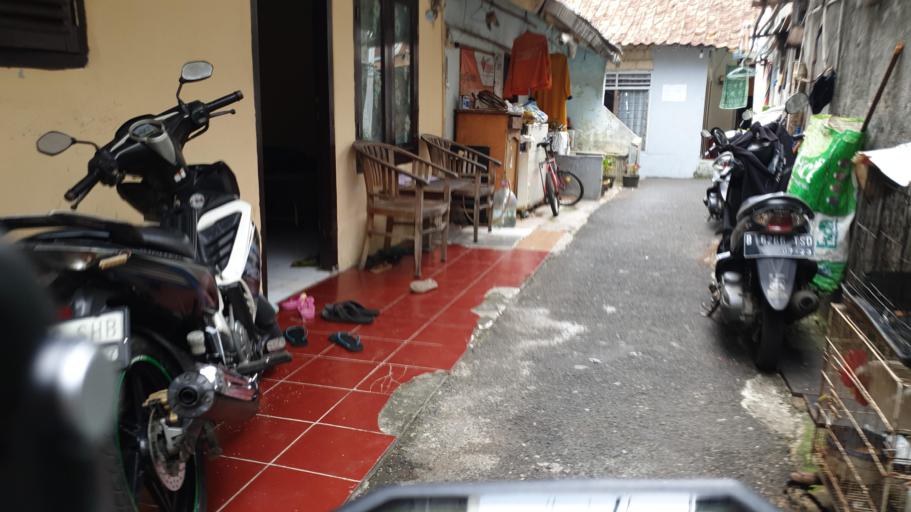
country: ID
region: Jakarta Raya
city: Jakarta
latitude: -6.2719
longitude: 106.7936
